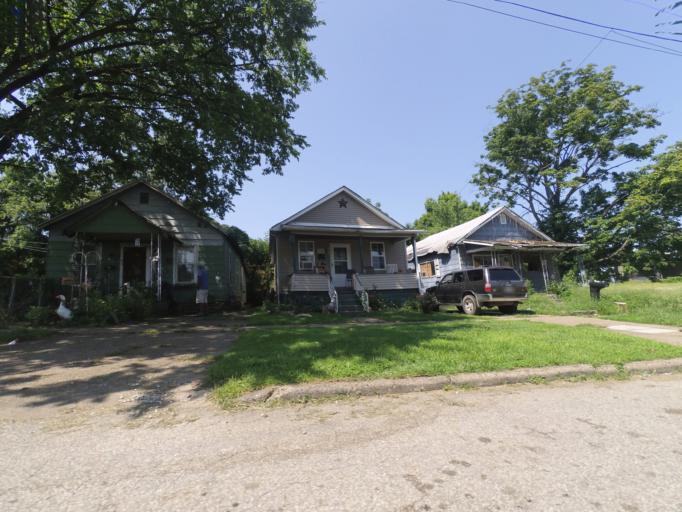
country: US
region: West Virginia
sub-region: Cabell County
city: Huntington
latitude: 38.4091
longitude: -82.4821
